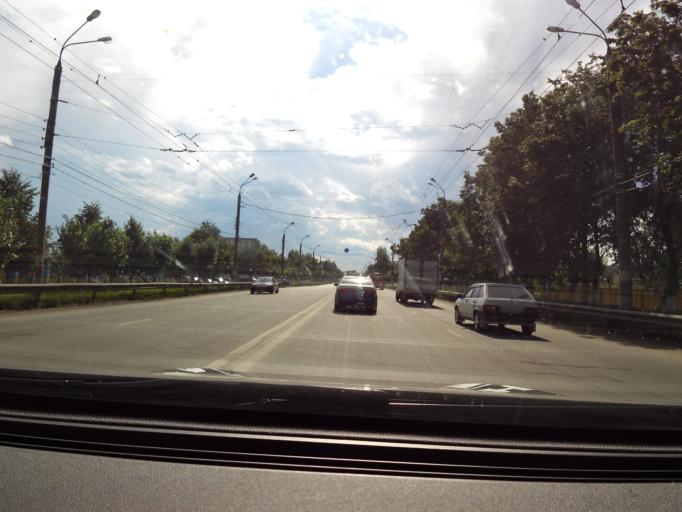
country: RU
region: Nizjnij Novgorod
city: Nizhniy Novgorod
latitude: 56.3172
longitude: 43.9163
